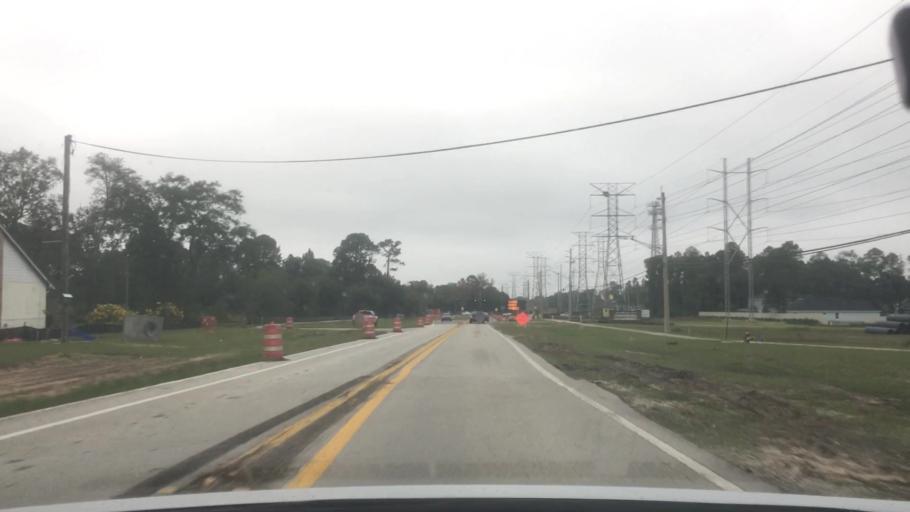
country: US
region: Florida
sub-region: Duval County
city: Atlantic Beach
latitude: 30.3563
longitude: -81.4901
